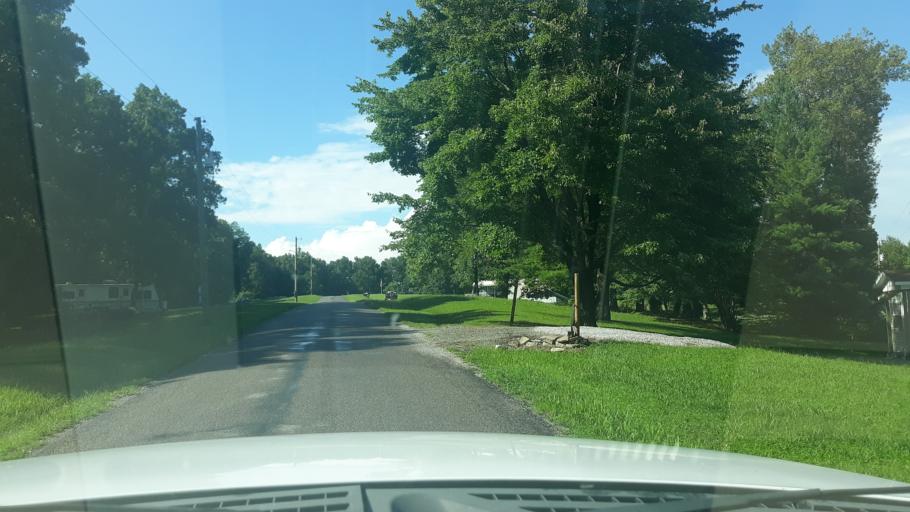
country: US
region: Illinois
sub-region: Saline County
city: Harrisburg
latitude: 37.8536
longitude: -88.5855
